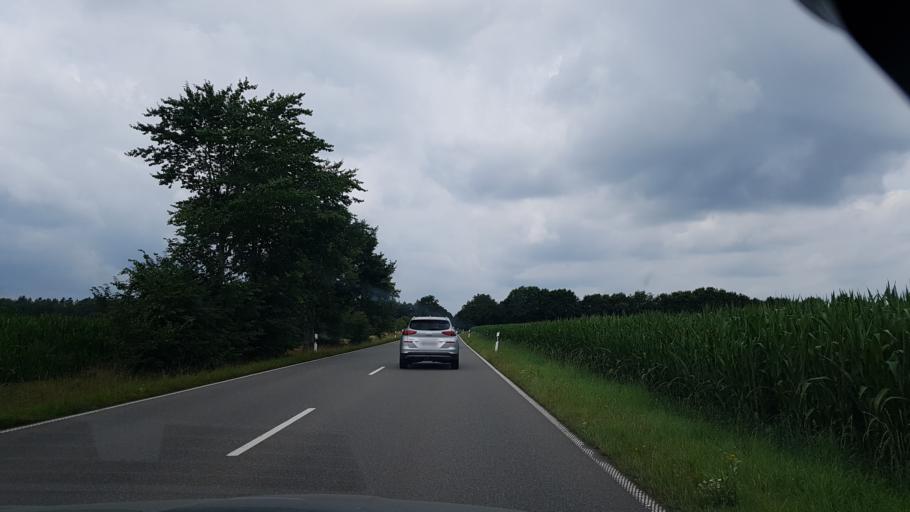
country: DE
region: Schleswig-Holstein
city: Gross Kummerfeld
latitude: 54.0234
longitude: 10.1128
